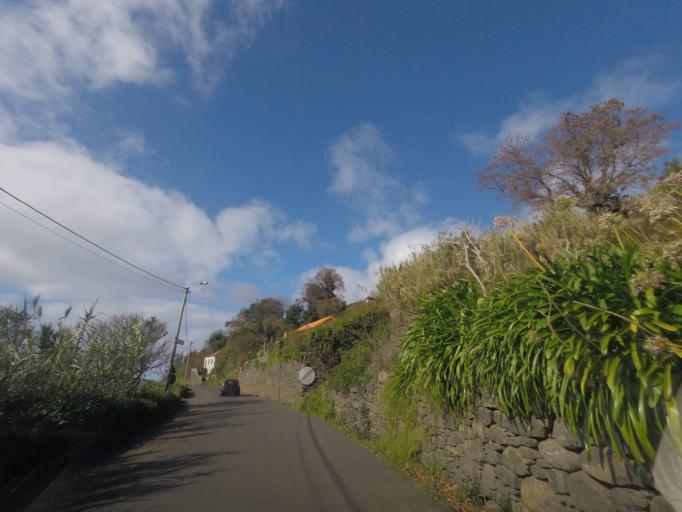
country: PT
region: Madeira
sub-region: Calheta
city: Faja da Ovelha
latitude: 32.7987
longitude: -17.2347
